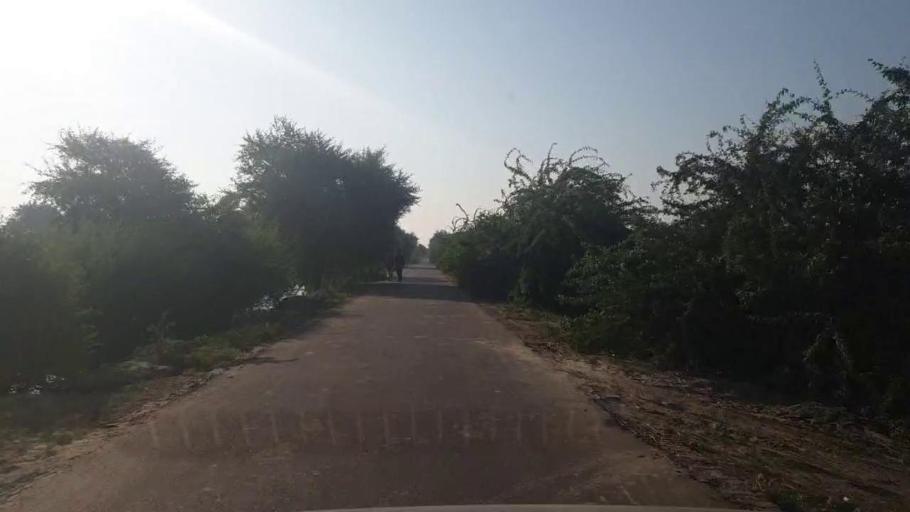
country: PK
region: Sindh
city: Tando Bago
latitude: 24.7288
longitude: 68.9369
